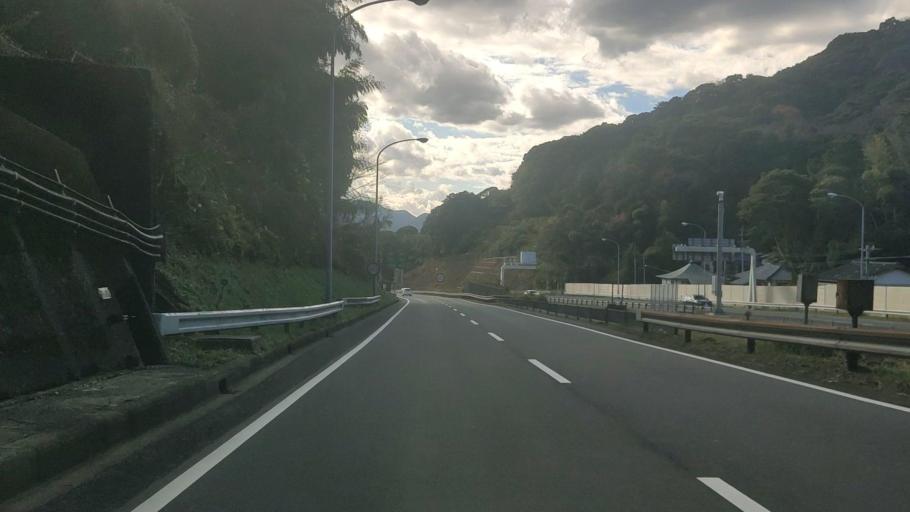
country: JP
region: Yamaguchi
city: Shimonoseki
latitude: 33.9165
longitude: 130.9633
